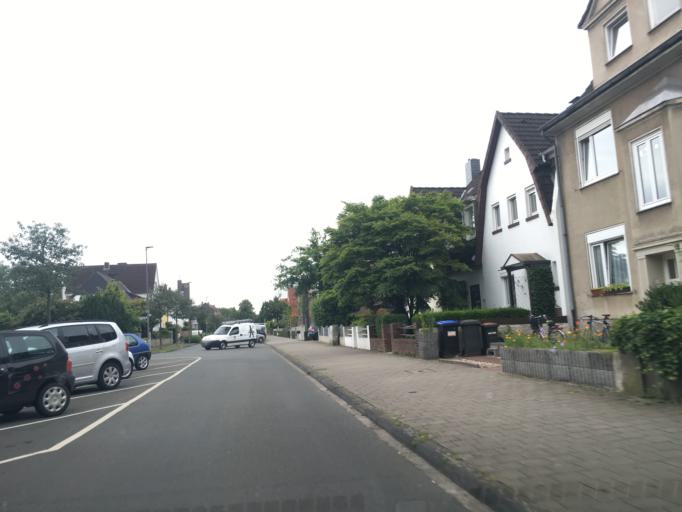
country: DE
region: North Rhine-Westphalia
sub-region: Regierungsbezirk Munster
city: Muenster
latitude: 51.9438
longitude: 7.6191
